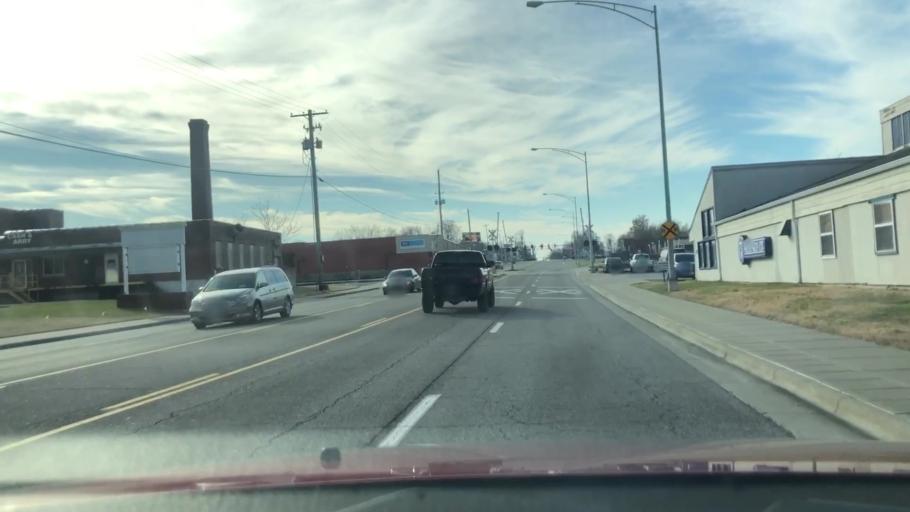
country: US
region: Missouri
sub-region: Greene County
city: Springfield
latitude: 37.2134
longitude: -93.2758
